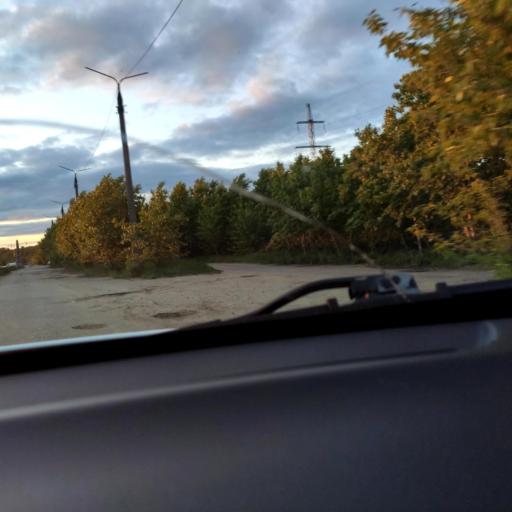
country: RU
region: Tatarstan
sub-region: Gorod Kazan'
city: Kazan
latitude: 55.7859
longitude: 49.0974
